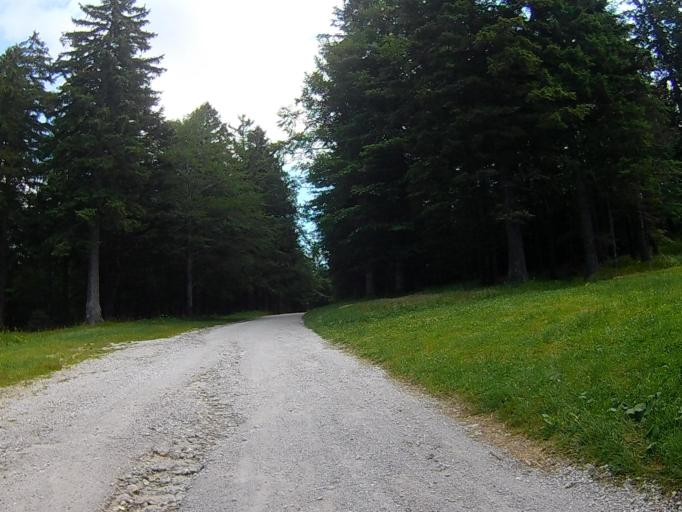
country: SI
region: Ruse
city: Ruse
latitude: 46.4984
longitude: 15.4965
